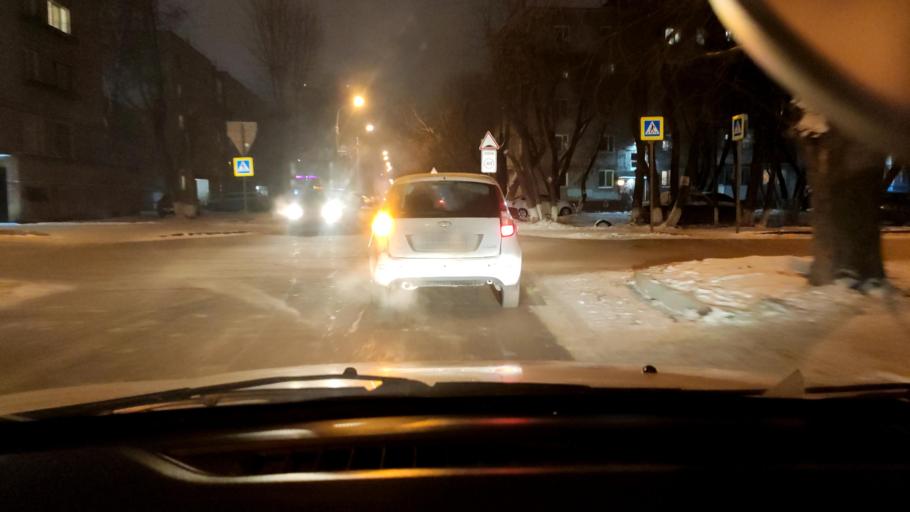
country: RU
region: Perm
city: Overyata
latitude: 58.0095
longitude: 55.9532
